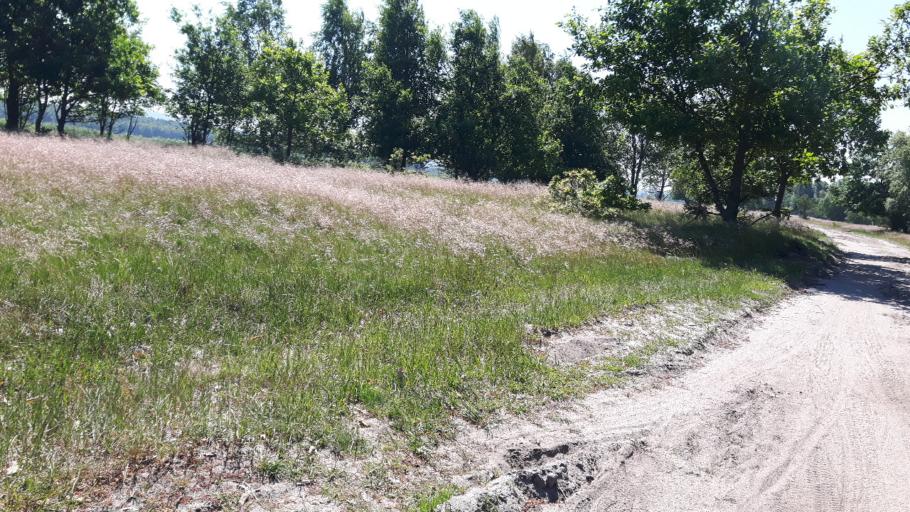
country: PL
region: Pomeranian Voivodeship
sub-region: Powiat slupski
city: Smoldzino
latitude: 54.6733
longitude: 17.1584
